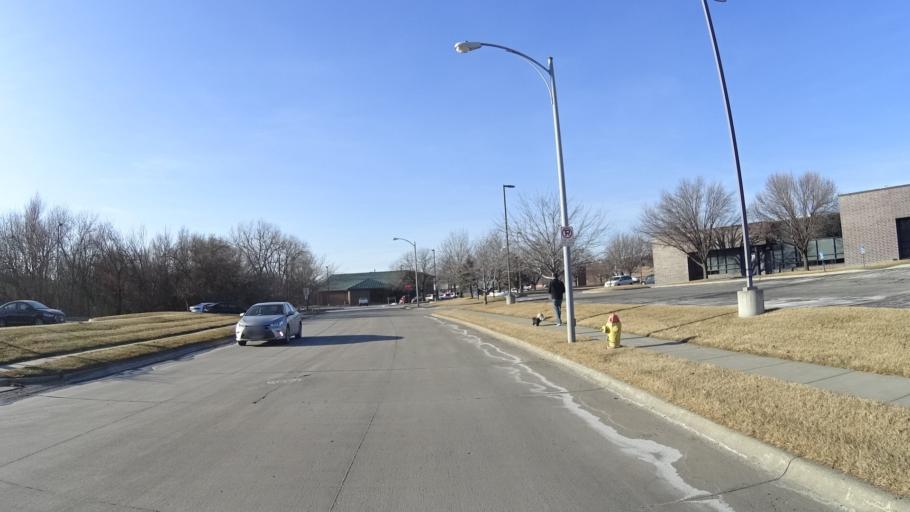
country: US
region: Nebraska
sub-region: Douglas County
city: Bennington
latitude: 41.2910
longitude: -96.1046
